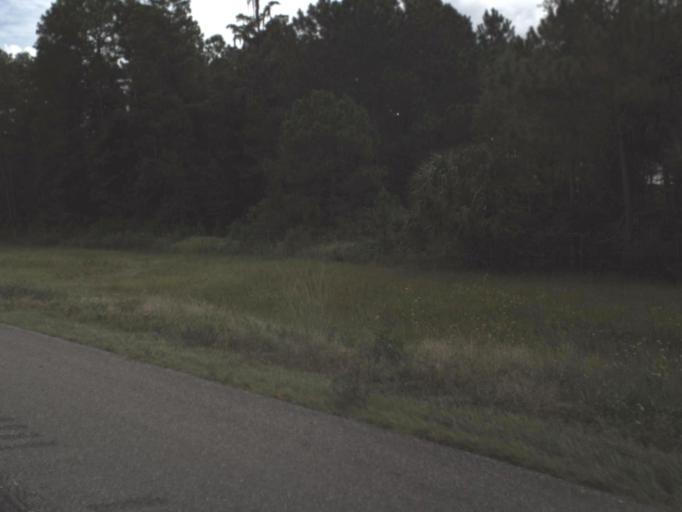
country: US
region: Florida
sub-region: Polk County
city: Davenport
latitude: 28.2223
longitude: -81.6630
